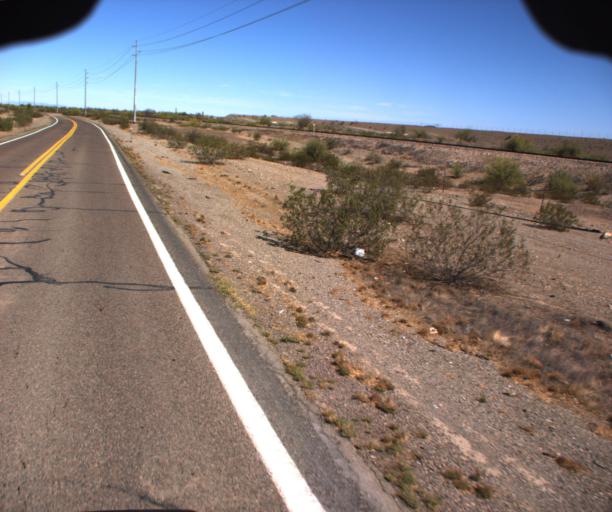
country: US
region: Arizona
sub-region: La Paz County
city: Salome
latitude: 33.7695
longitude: -113.7920
